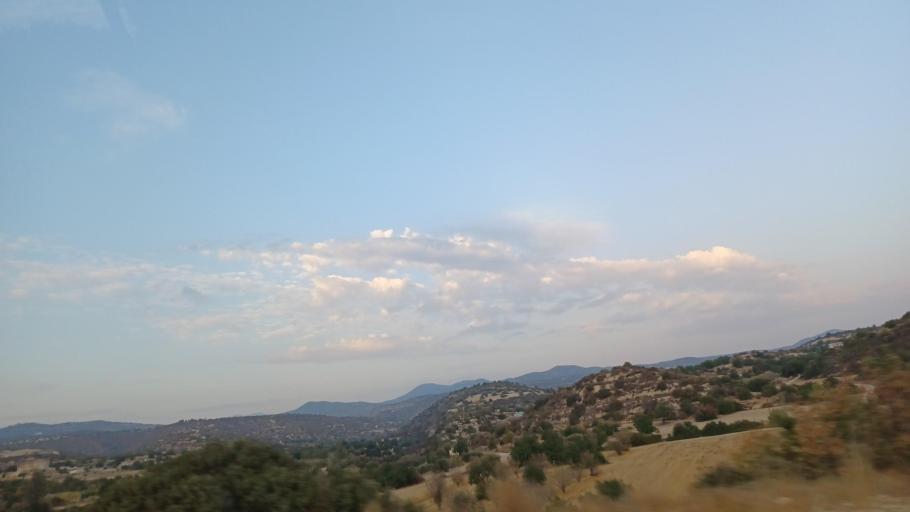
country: CY
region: Limassol
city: Pano Polemidia
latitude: 34.7544
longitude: 32.9721
